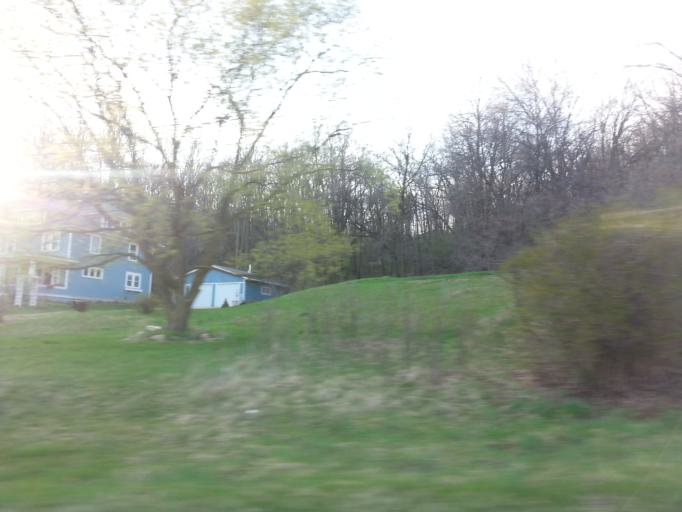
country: US
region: Wisconsin
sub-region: Pierce County
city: River Falls
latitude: 44.8831
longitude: -92.6810
